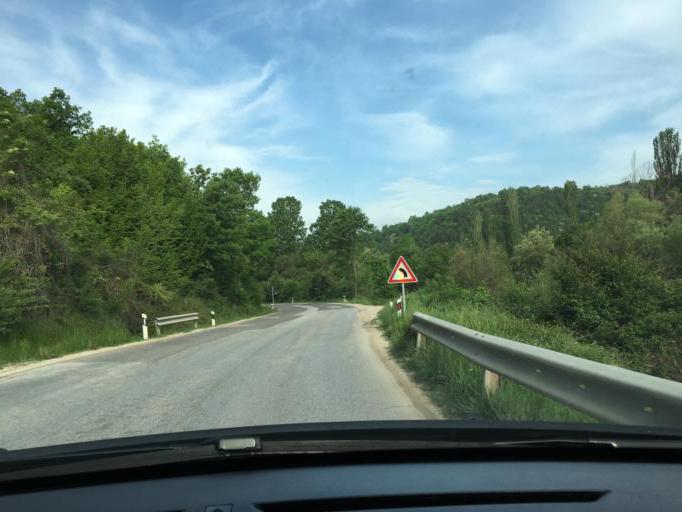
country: MK
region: Kriva Palanka
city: Kriva Palanka
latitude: 42.1893
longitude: 22.2941
